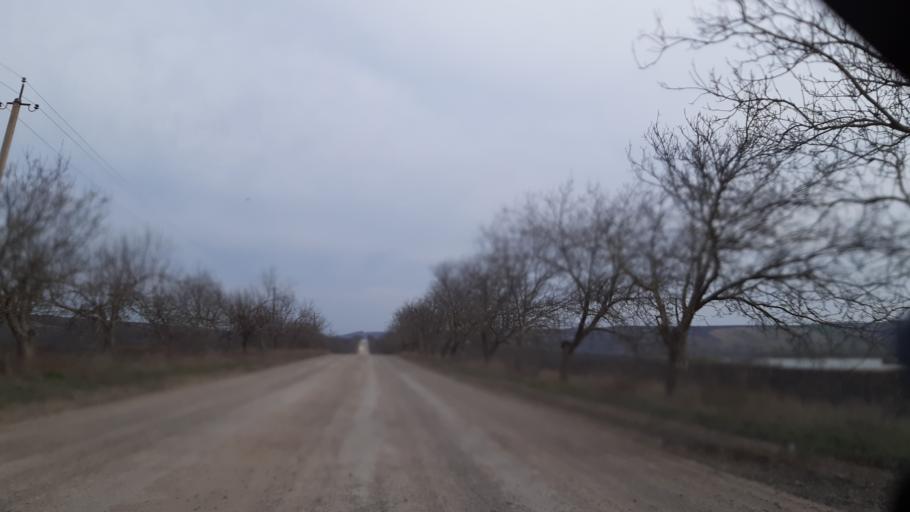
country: MD
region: Soldanesti
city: Soldanesti
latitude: 47.6999
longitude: 28.7240
